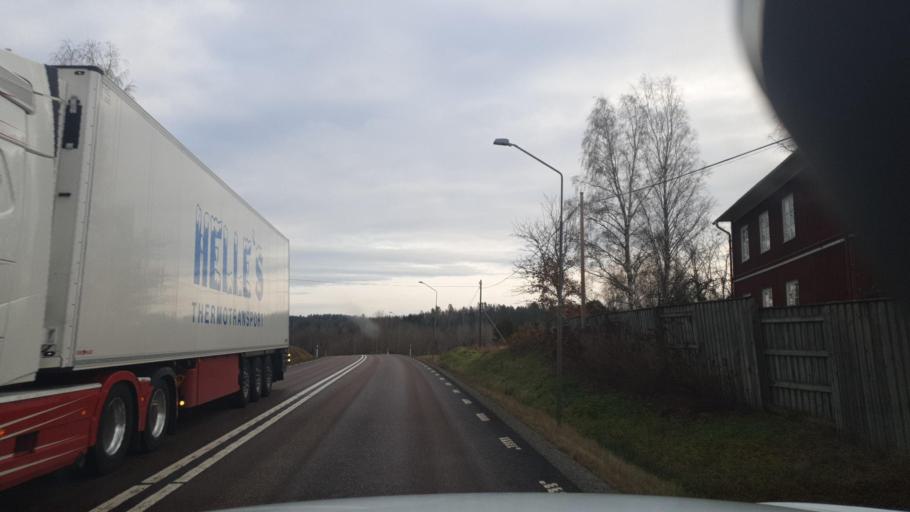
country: SE
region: Vaermland
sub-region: Arvika Kommun
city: Arvika
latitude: 59.6636
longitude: 12.8900
